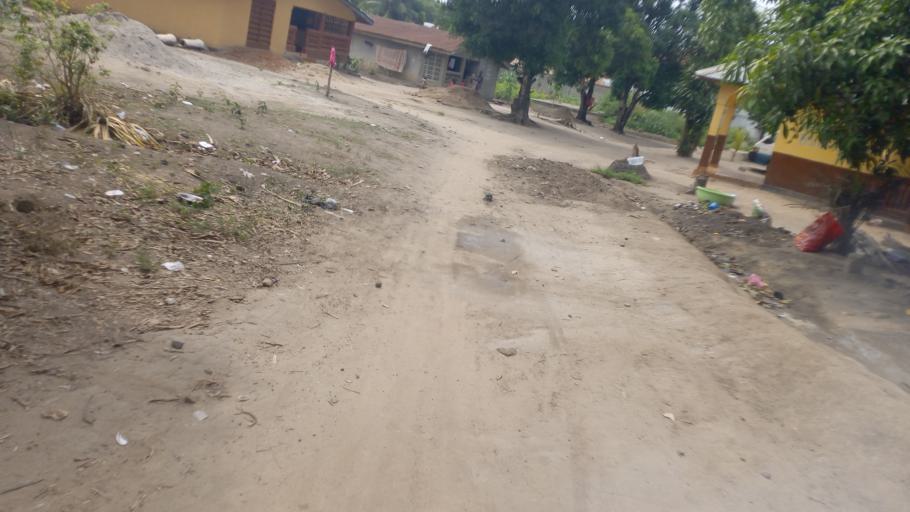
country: SL
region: Western Area
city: Waterloo
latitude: 8.3101
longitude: -13.0636
